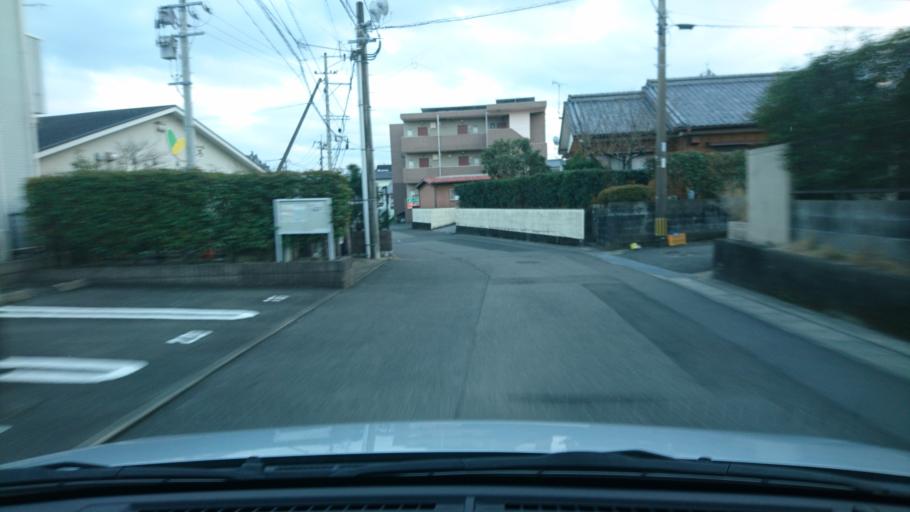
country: JP
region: Miyazaki
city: Miyazaki-shi
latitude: 31.8560
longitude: 131.4308
